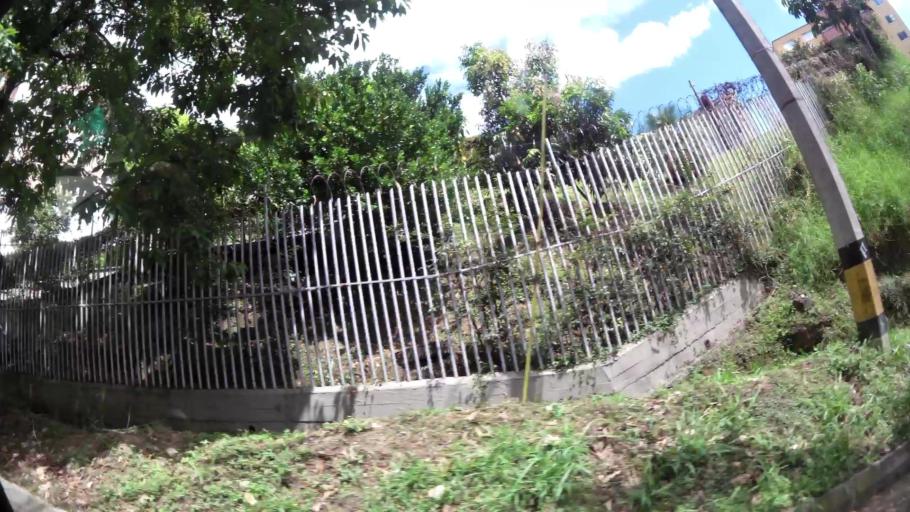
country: CO
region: Antioquia
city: Sabaneta
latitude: 6.1453
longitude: -75.6154
